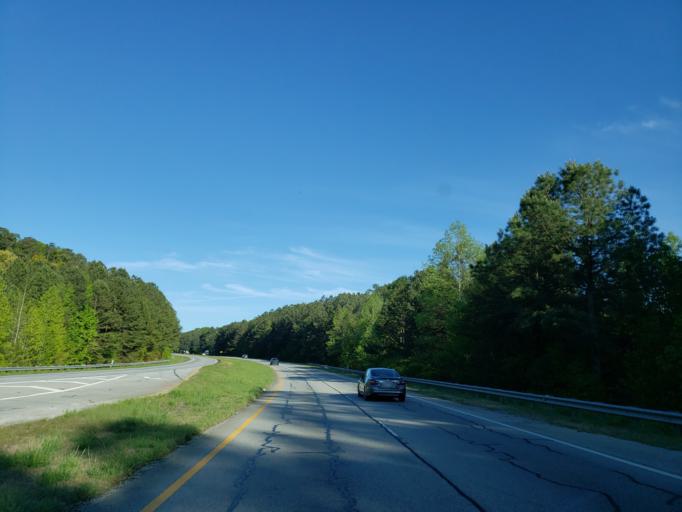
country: US
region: Georgia
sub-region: Paulding County
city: Dallas
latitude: 33.9159
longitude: -84.9240
